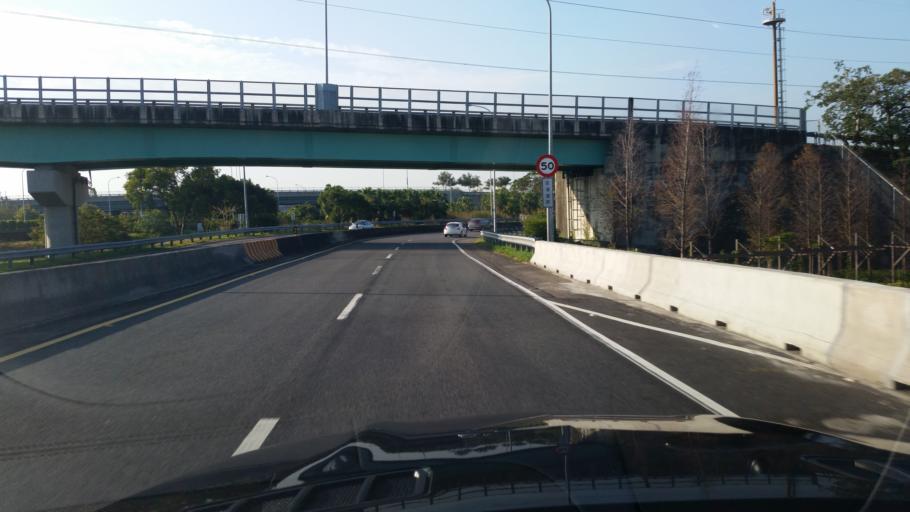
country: TW
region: Taiwan
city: Fengyuan
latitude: 24.3142
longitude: 120.7019
